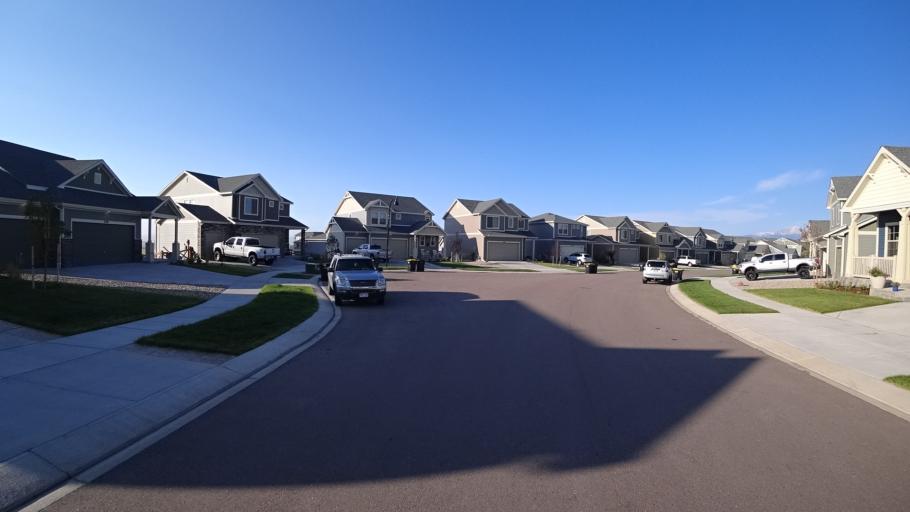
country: US
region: Colorado
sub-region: El Paso County
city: Cimarron Hills
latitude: 38.9288
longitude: -104.6532
